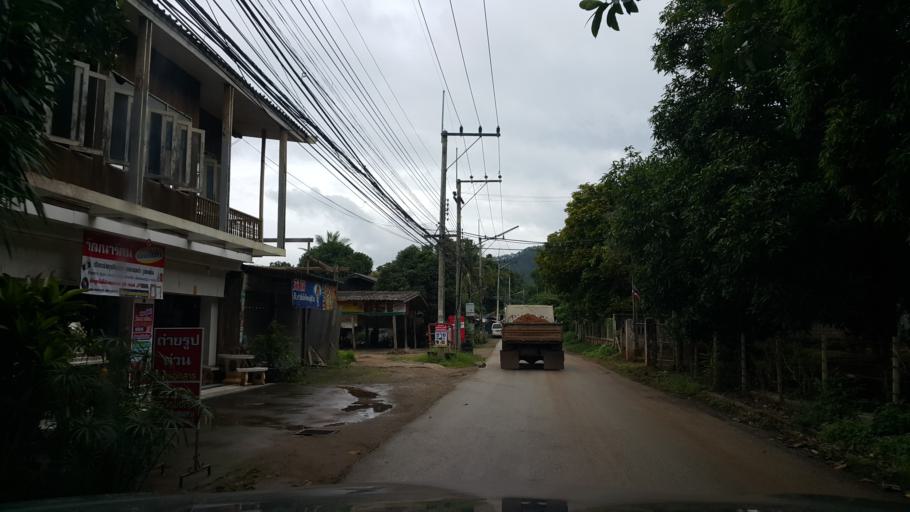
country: TH
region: Chiang Mai
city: Samoeng
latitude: 18.8506
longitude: 98.7320
